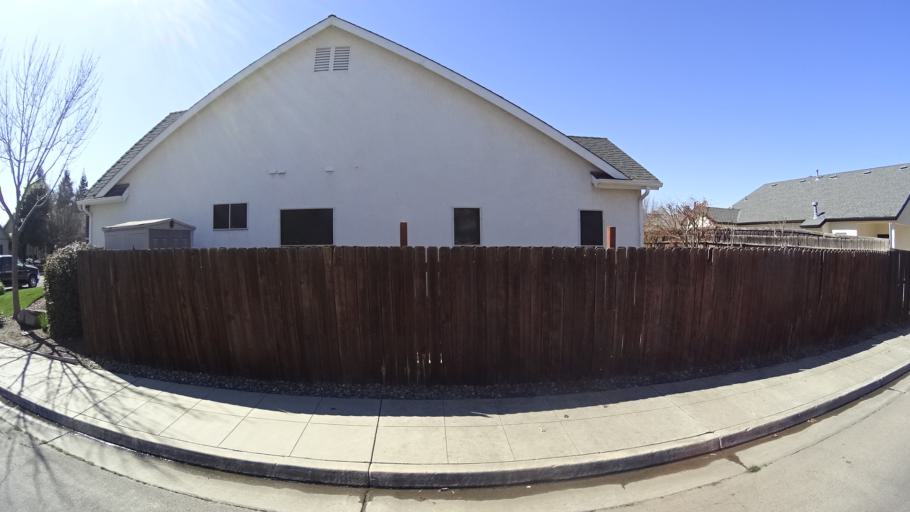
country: US
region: California
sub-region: Fresno County
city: Clovis
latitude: 36.8651
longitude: -119.7364
